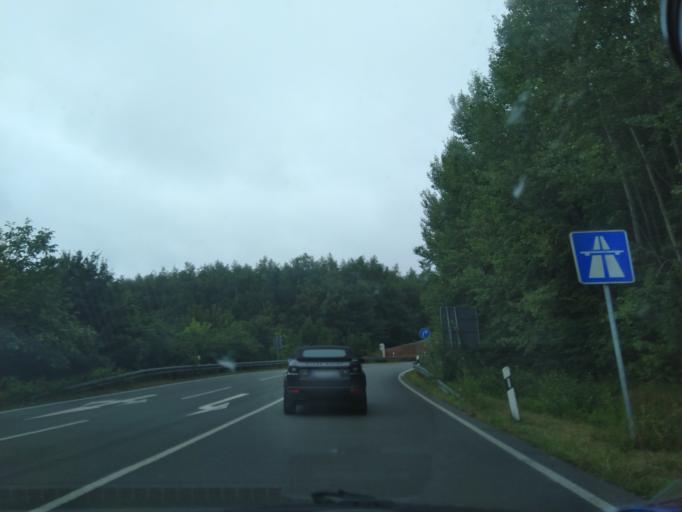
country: DE
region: Lower Saxony
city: Osnabrueck
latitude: 52.2435
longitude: 8.0344
